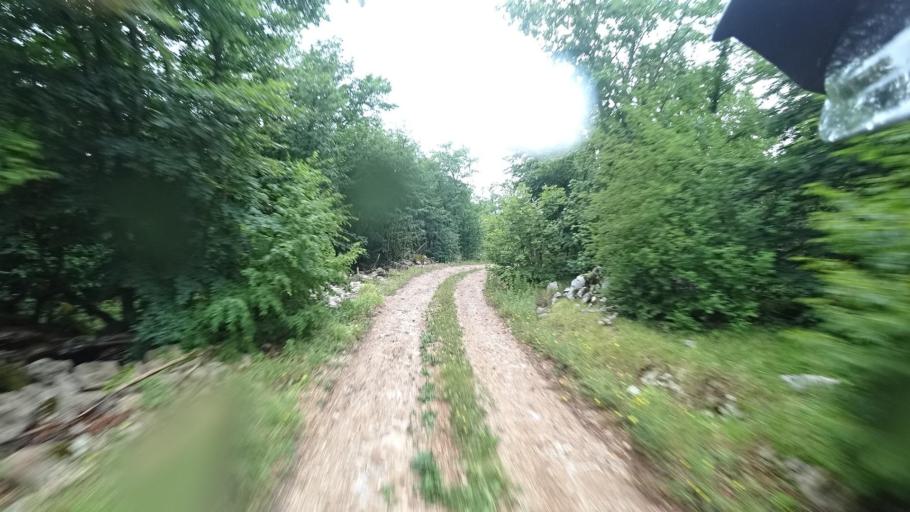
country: HR
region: Licko-Senjska
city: Jezerce
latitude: 44.7252
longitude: 15.6490
